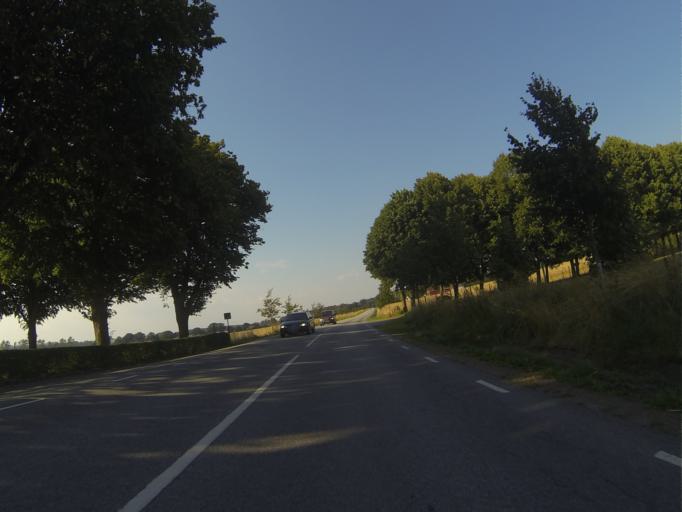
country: SE
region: Skane
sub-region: Lunds Kommun
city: Genarp
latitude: 55.6151
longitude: 13.4053
